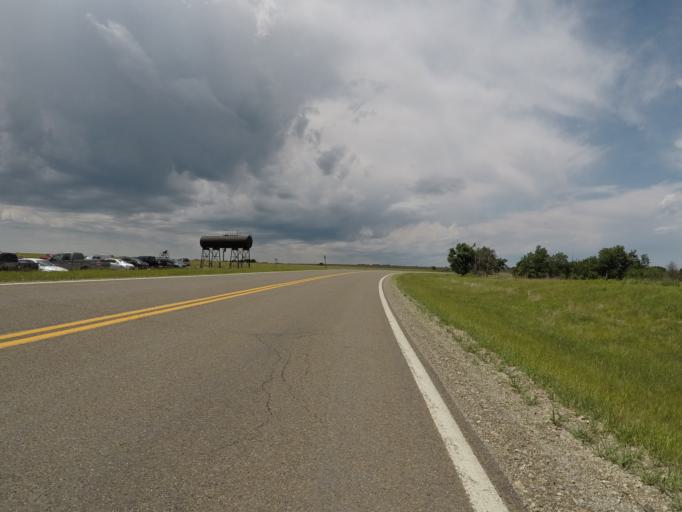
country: US
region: Kansas
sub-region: Wabaunsee County
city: Alma
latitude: 38.8559
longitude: -96.3746
